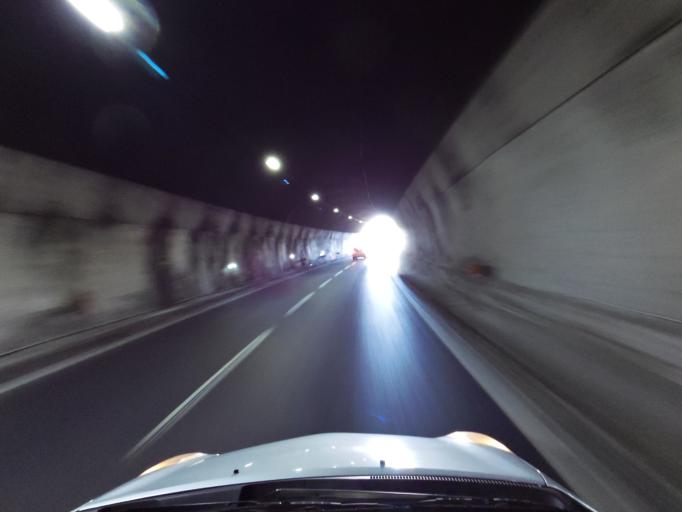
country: IT
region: Tuscany
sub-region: Province of Florence
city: Cavallina
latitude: 43.9466
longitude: 11.2153
